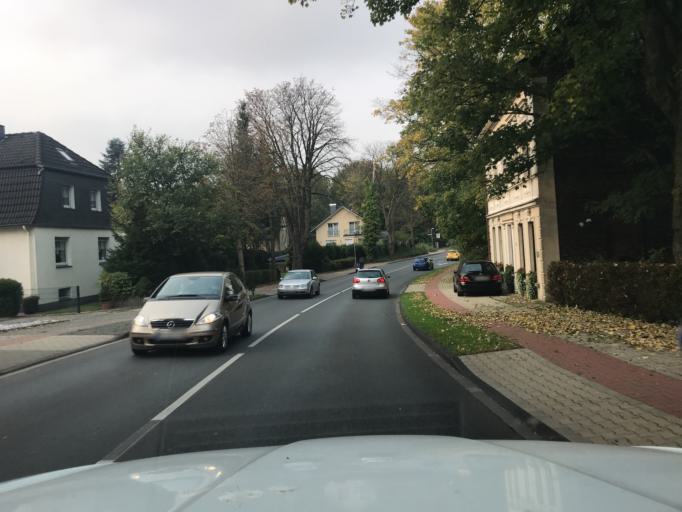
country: DE
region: North Rhine-Westphalia
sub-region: Regierungsbezirk Dusseldorf
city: Velbert
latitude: 51.3516
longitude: 7.0225
